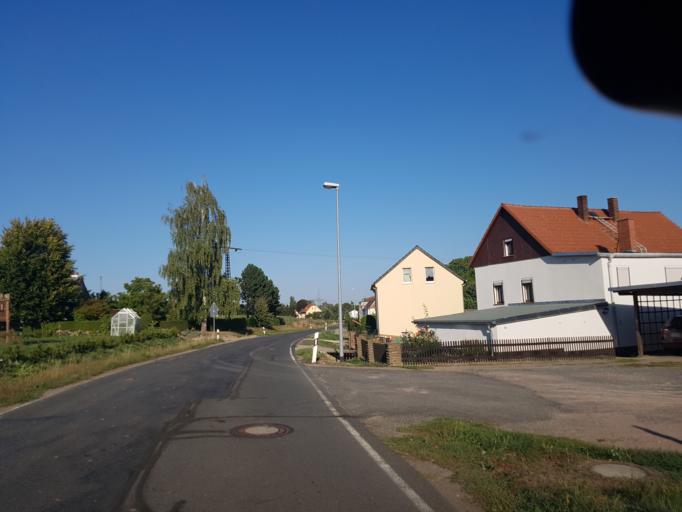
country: DE
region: Saxony
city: Ostrau
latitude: 51.1958
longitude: 13.1436
